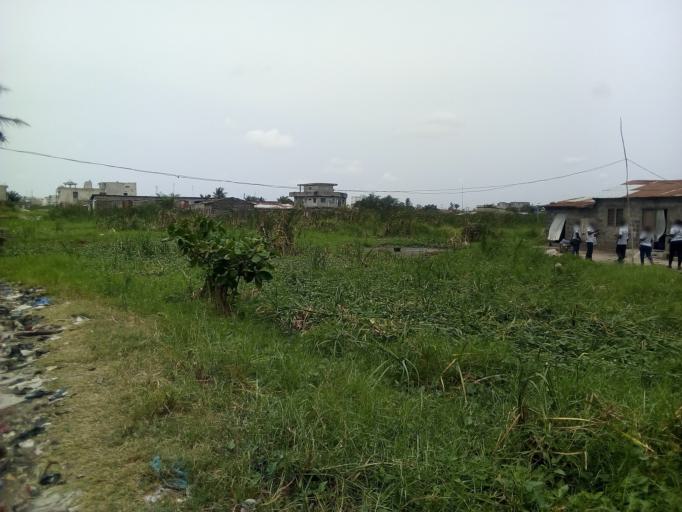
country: BJ
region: Littoral
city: Cotonou
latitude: 6.3886
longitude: 2.4305
